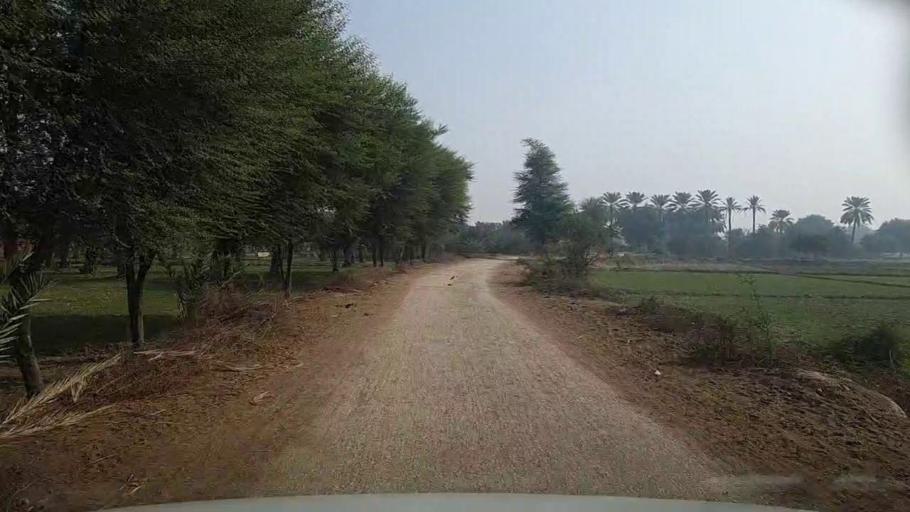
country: PK
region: Sindh
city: Setharja Old
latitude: 27.1422
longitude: 68.4939
